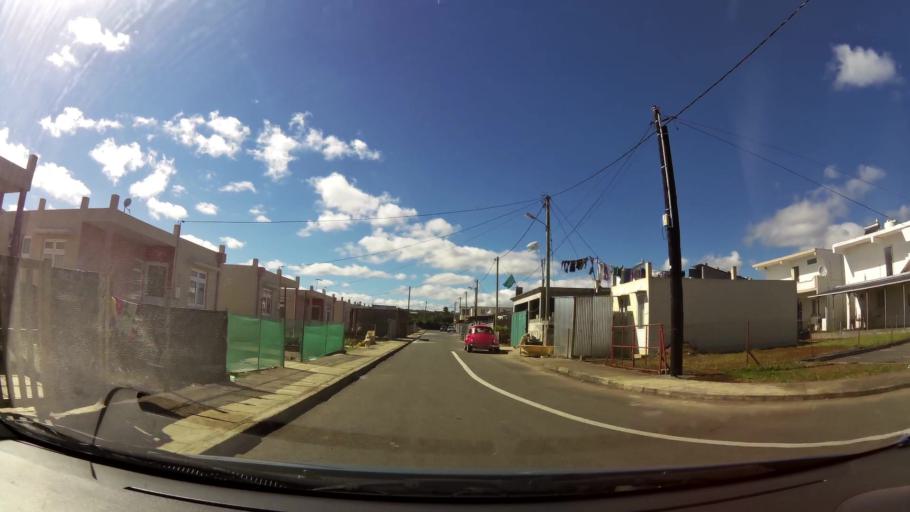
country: MU
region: Plaines Wilhems
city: Vacoas
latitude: -20.3291
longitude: 57.4819
